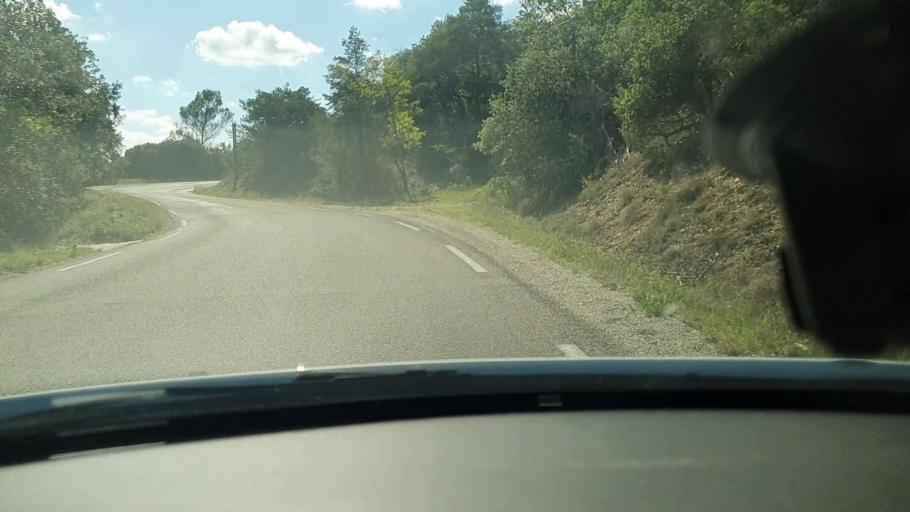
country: FR
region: Languedoc-Roussillon
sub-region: Departement du Gard
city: Goudargues
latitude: 44.1719
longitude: 4.4878
